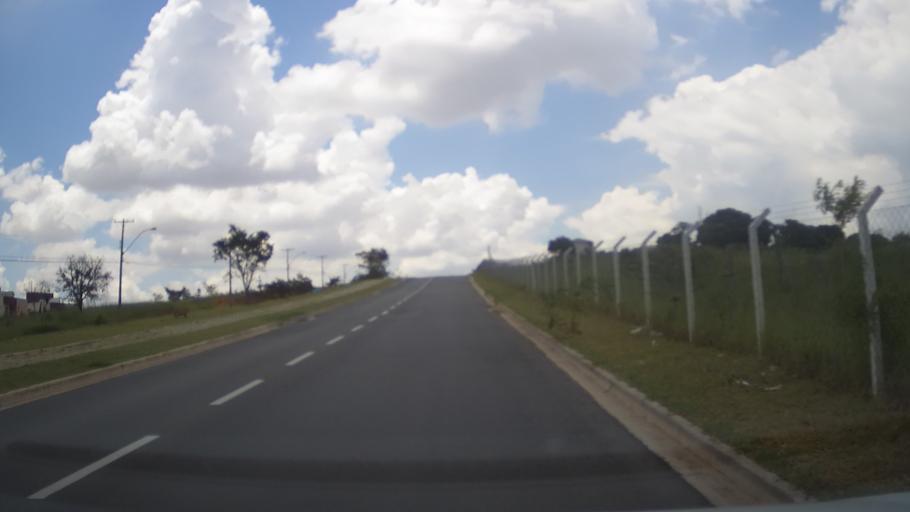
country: BR
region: Sao Paulo
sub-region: Valinhos
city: Valinhos
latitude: -22.9886
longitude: -46.9949
